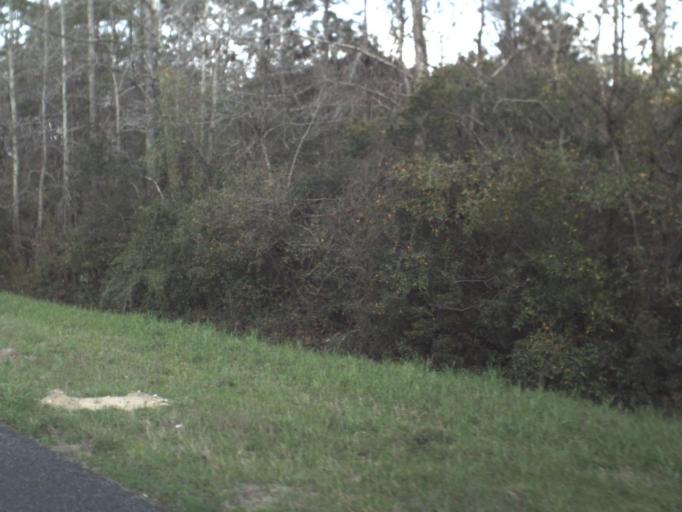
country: US
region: Florida
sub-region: Bay County
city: Youngstown
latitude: 30.4685
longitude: -85.4222
